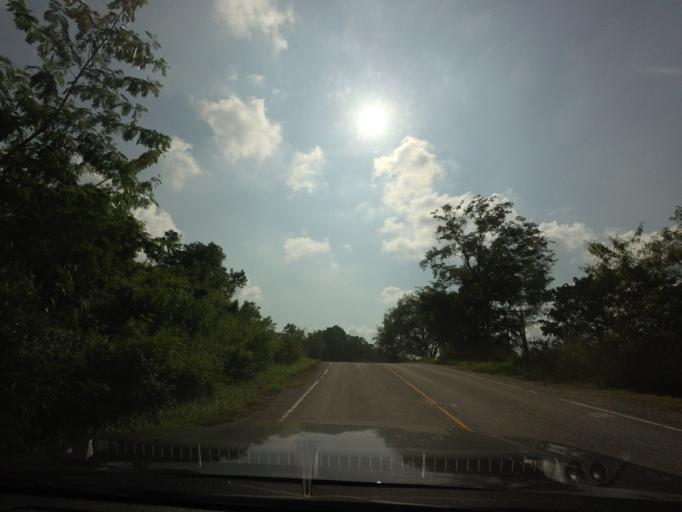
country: TH
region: Nan
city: Santi Suk
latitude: 18.9823
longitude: 100.9976
